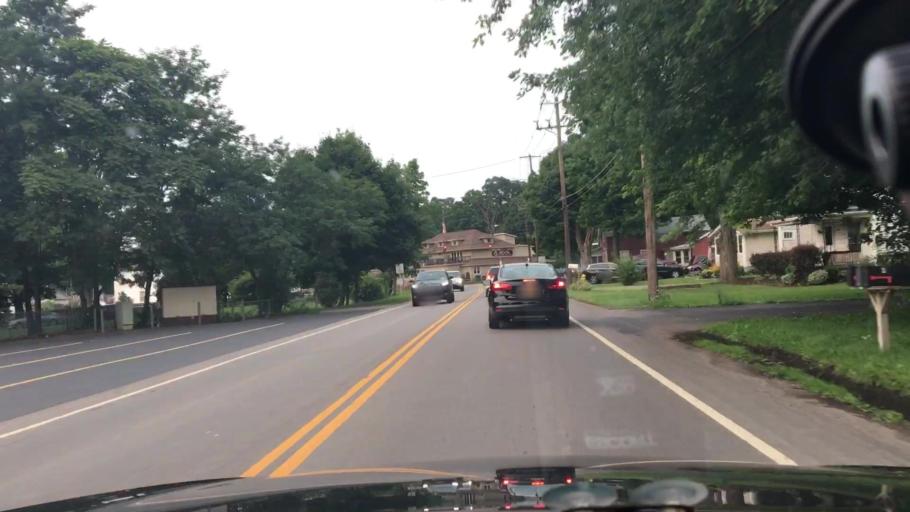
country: US
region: New York
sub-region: Erie County
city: Hamburg
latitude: 42.7396
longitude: -78.7995
